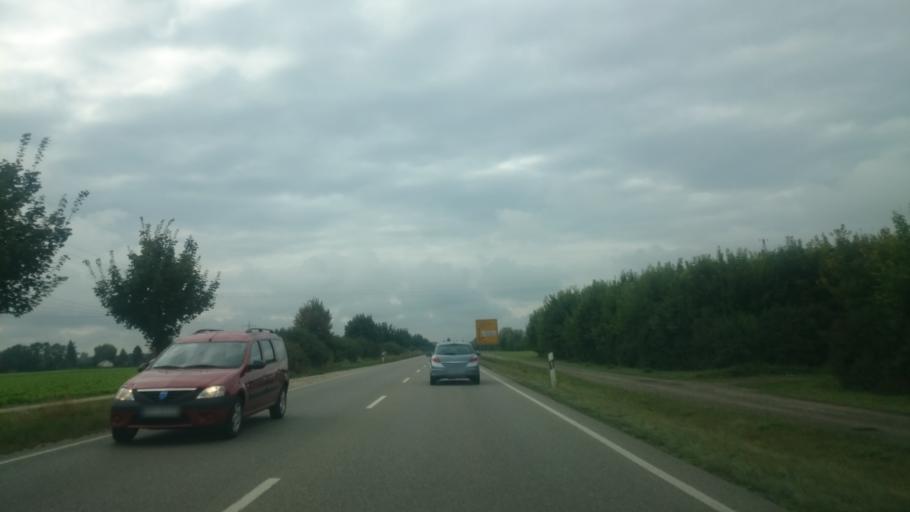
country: DE
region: Bavaria
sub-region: Swabia
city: Friedberg
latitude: 48.3689
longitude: 10.9595
